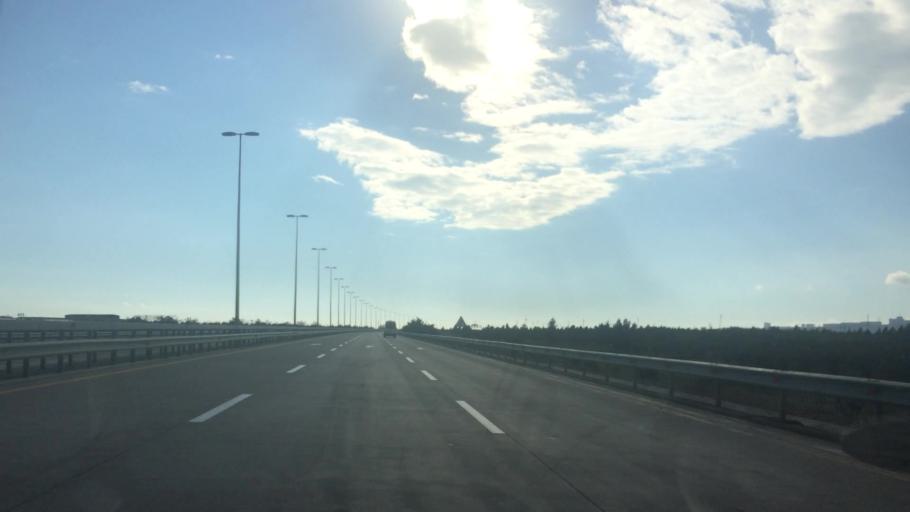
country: AZ
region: Baki
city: Hovsan
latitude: 40.3831
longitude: 50.0612
